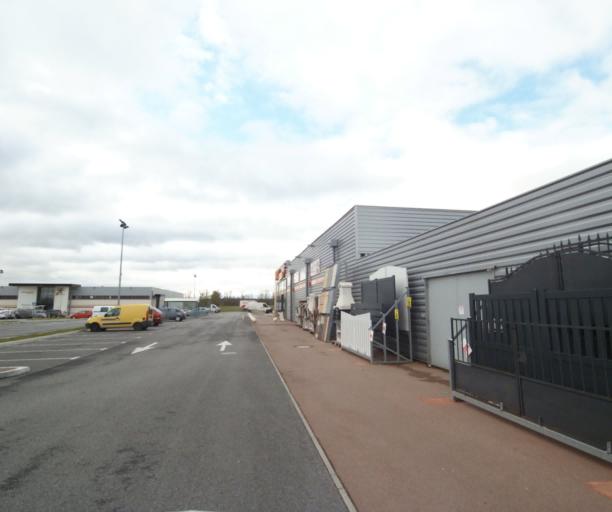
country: FR
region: Midi-Pyrenees
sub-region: Departement de l'Ariege
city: Saverdun
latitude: 43.2513
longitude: 1.5641
